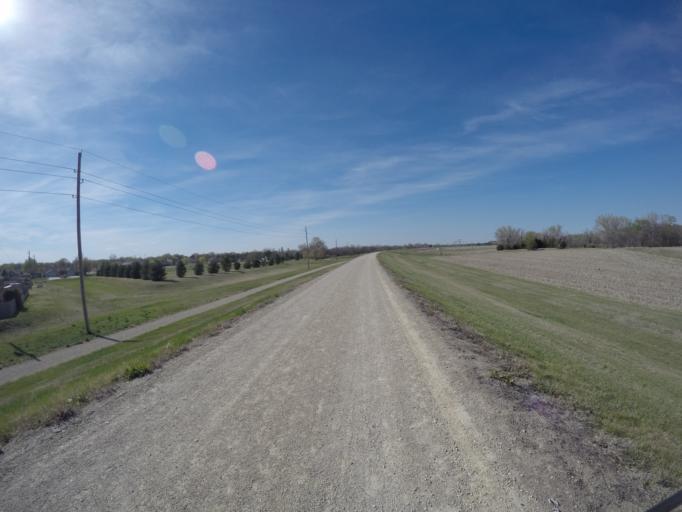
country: US
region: Kansas
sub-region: Saline County
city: Salina
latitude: 38.8217
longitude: -97.5858
